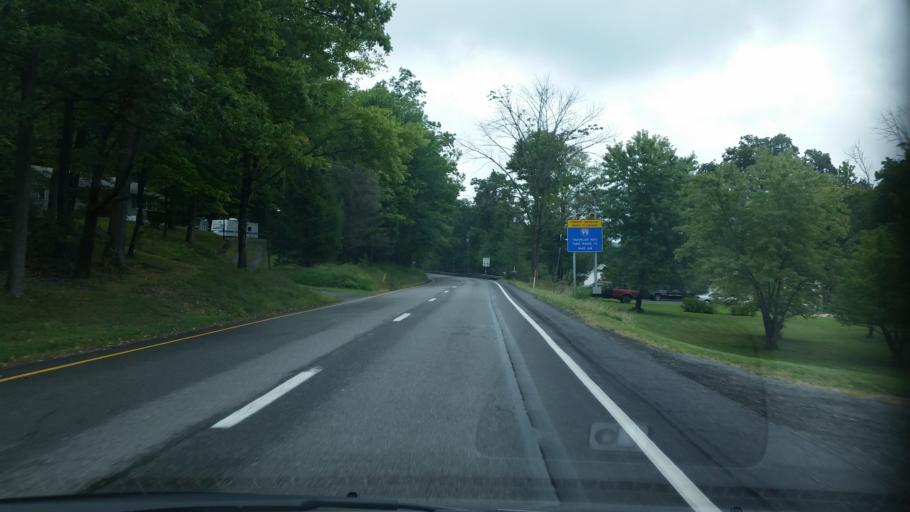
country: US
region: Pennsylvania
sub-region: Centre County
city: Stormstown
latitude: 40.8219
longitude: -78.1020
